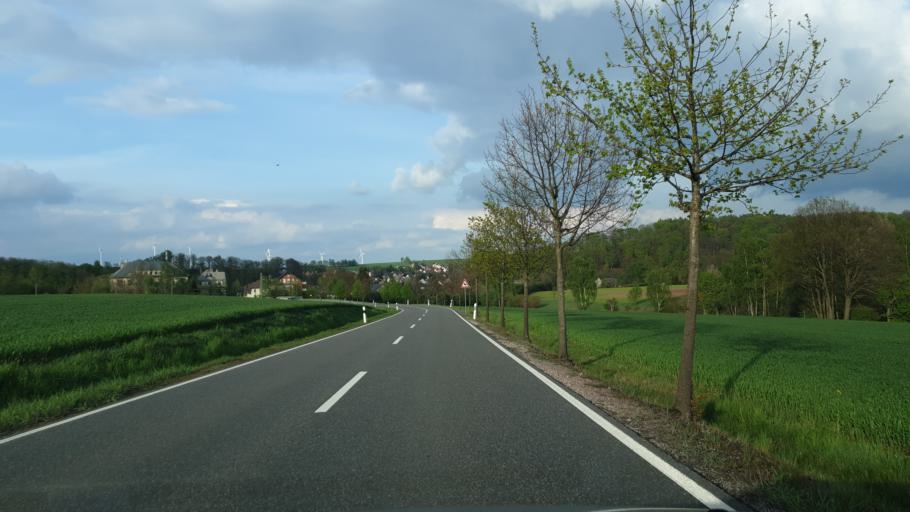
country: DE
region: Saxony
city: Lichtenstein
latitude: 50.7407
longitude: 12.6499
